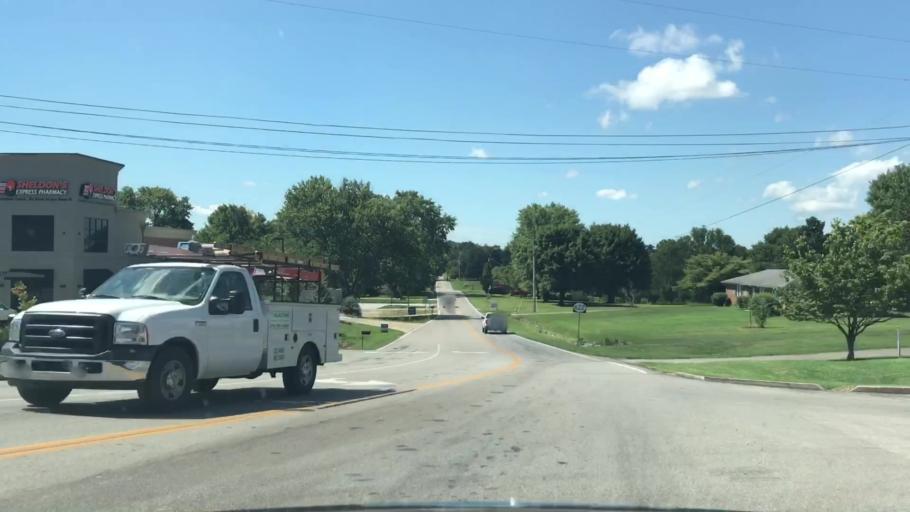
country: US
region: Kentucky
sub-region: Warren County
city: Plano
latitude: 36.9199
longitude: -86.4090
